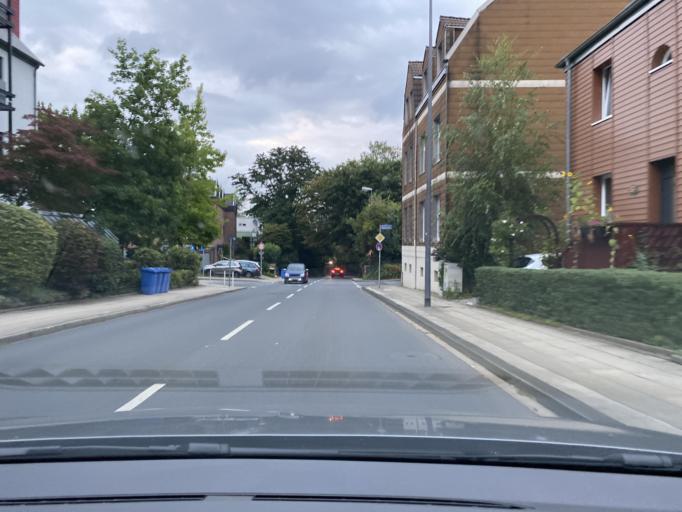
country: DE
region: North Rhine-Westphalia
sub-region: Regierungsbezirk Dusseldorf
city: Essen
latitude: 51.4358
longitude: 7.0777
